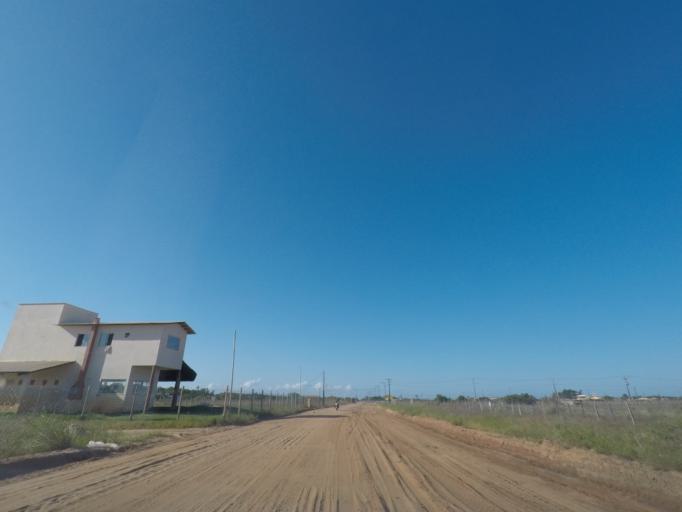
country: BR
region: Bahia
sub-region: Camamu
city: Camamu
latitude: -13.9371
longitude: -38.9467
